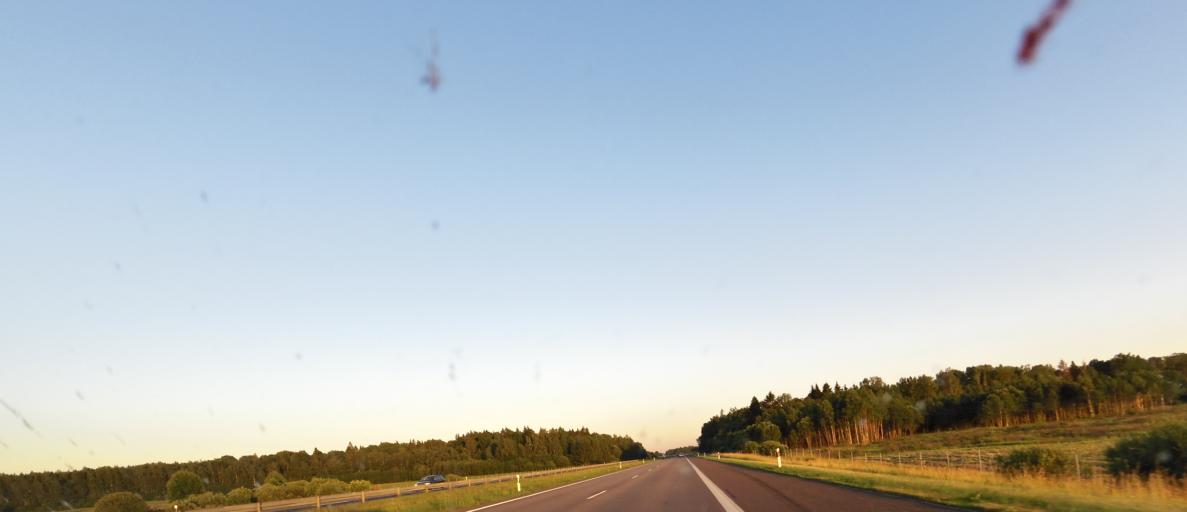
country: LT
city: Sirvintos
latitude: 54.9954
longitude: 24.9267
